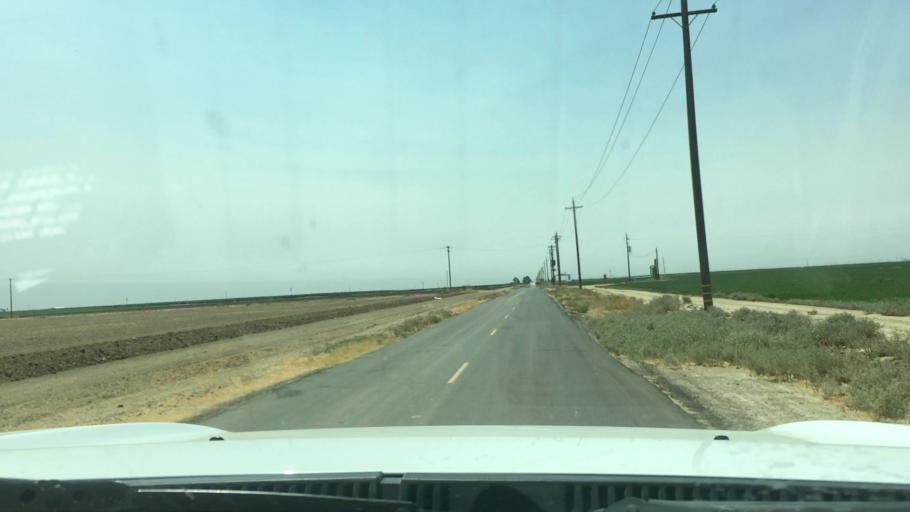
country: US
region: California
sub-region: Tulare County
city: Alpaugh
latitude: 35.7557
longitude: -119.4369
